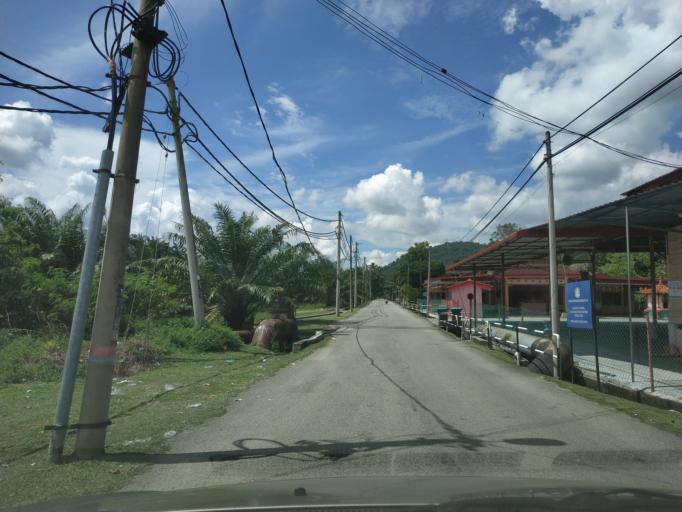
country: MY
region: Perak
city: Parit Buntar
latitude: 5.1384
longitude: 100.5930
